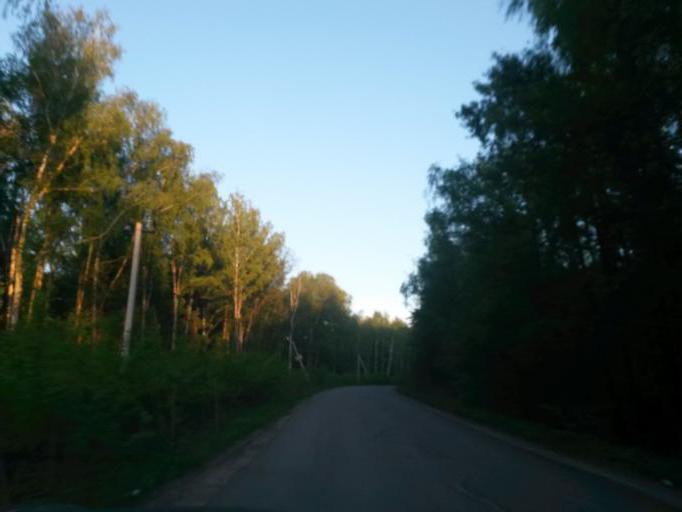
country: RU
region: Moskovskaya
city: L'vovskiy
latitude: 55.3158
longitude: 37.6142
